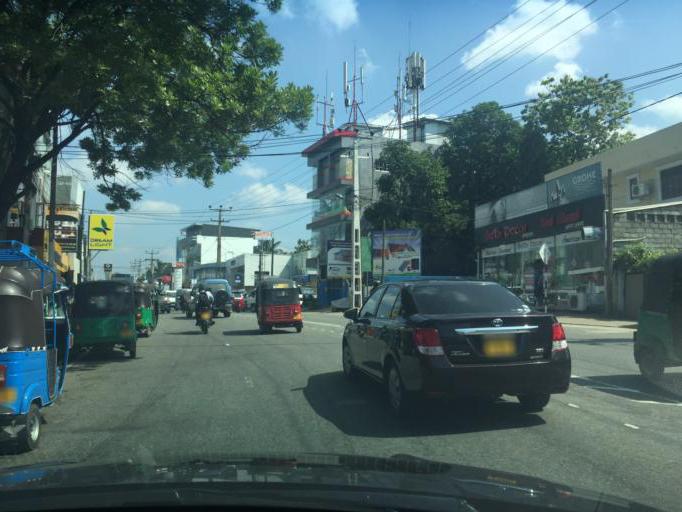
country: LK
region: Western
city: Pita Kotte
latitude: 6.8827
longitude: 79.8870
